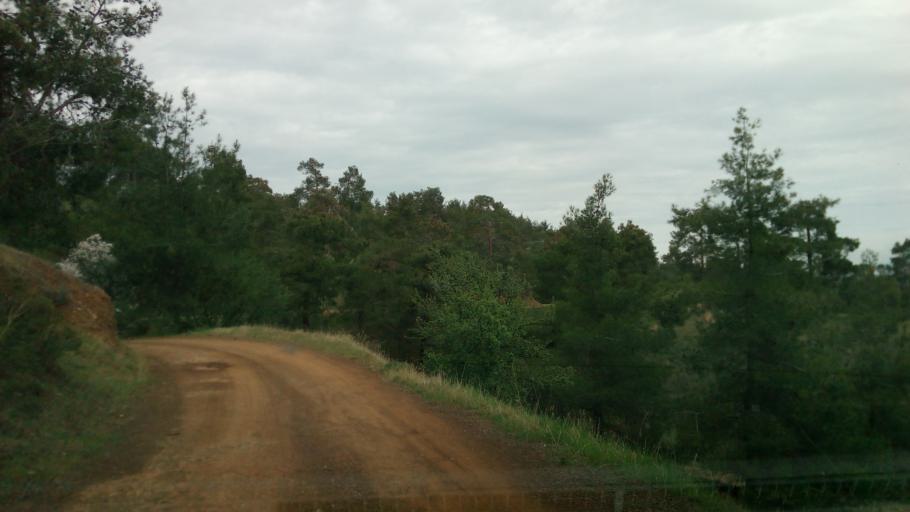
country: CY
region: Lefkosia
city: Klirou
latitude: 35.0021
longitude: 33.1058
